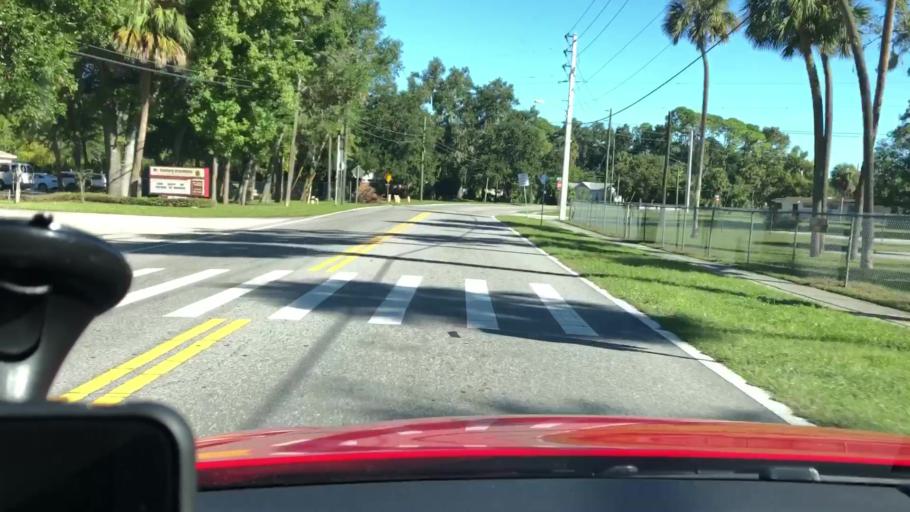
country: US
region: Florida
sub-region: Volusia County
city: Daytona Beach
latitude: 29.1934
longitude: -81.0237
